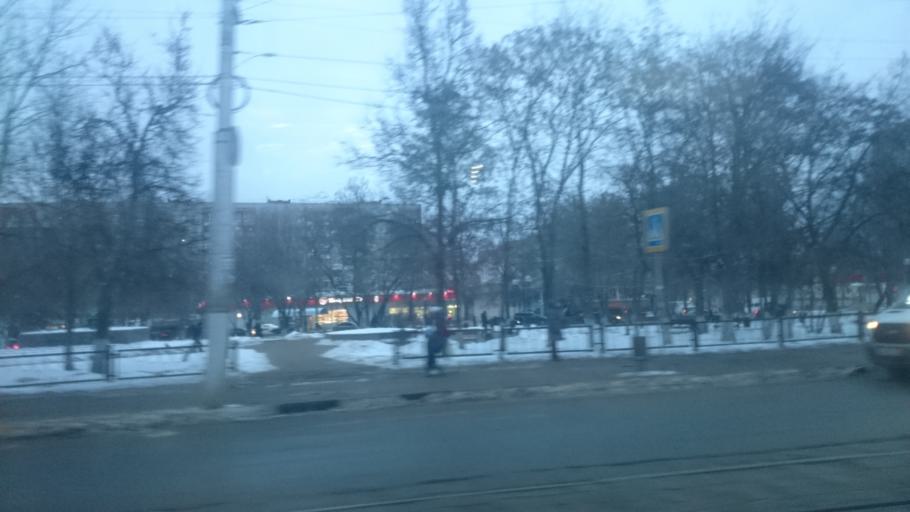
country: RU
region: Tula
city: Tula
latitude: 54.1774
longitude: 37.6291
